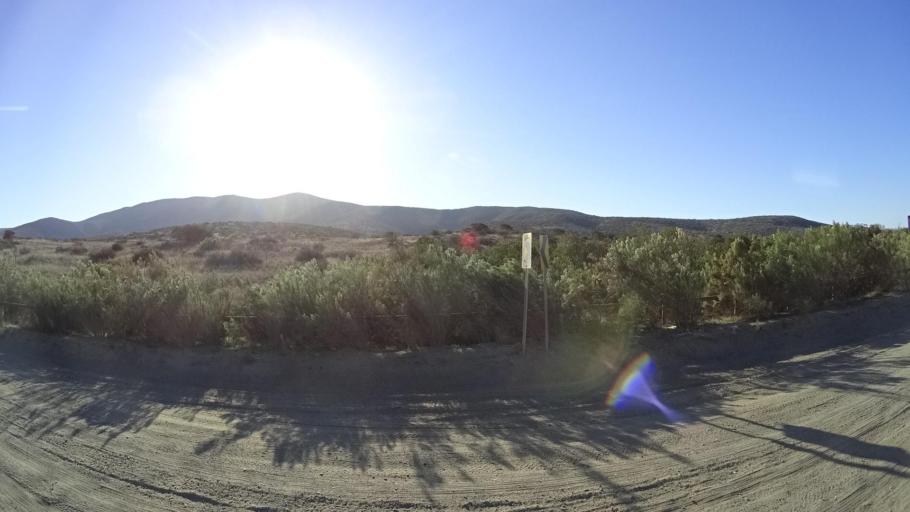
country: US
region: California
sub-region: San Diego County
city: Jamul
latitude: 32.6639
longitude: -116.9286
